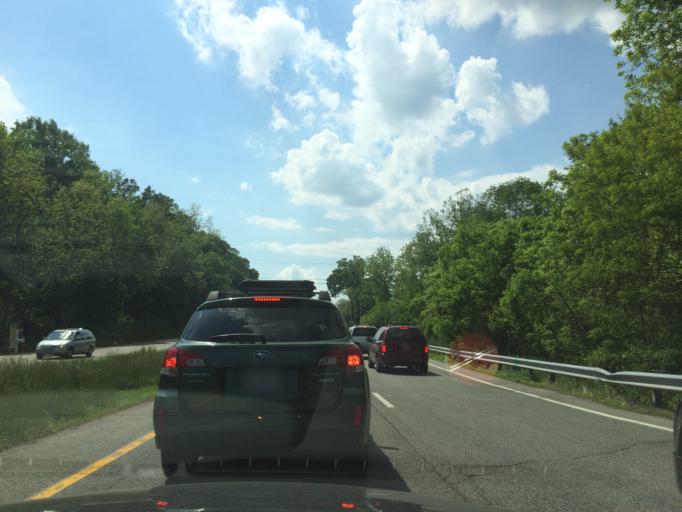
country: US
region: Maryland
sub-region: Howard County
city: Columbia
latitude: 39.2790
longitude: -76.8533
